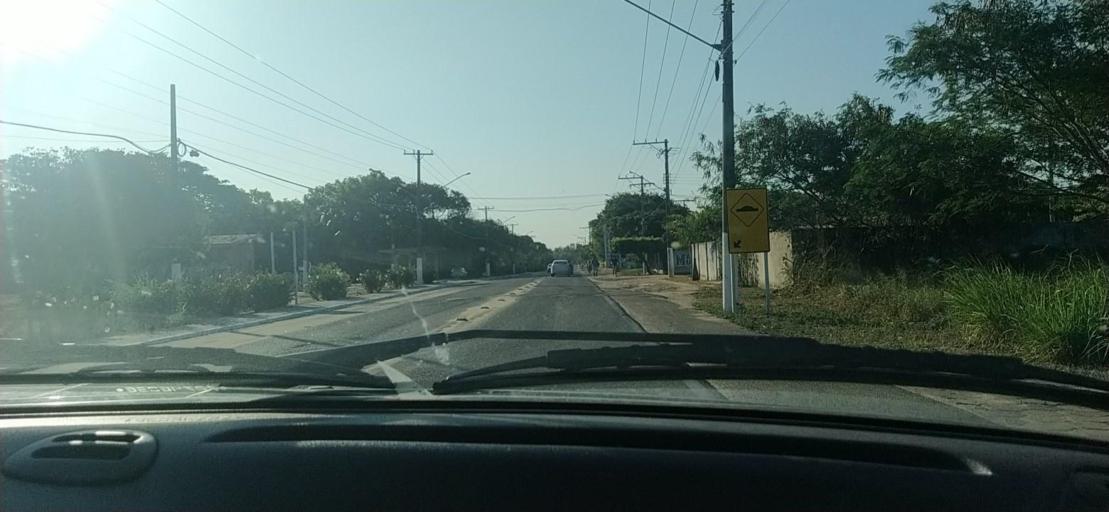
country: BR
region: Espirito Santo
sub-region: Conceicao Da Barra
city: Conceicao da Barra
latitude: -18.5709
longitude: -39.7390
